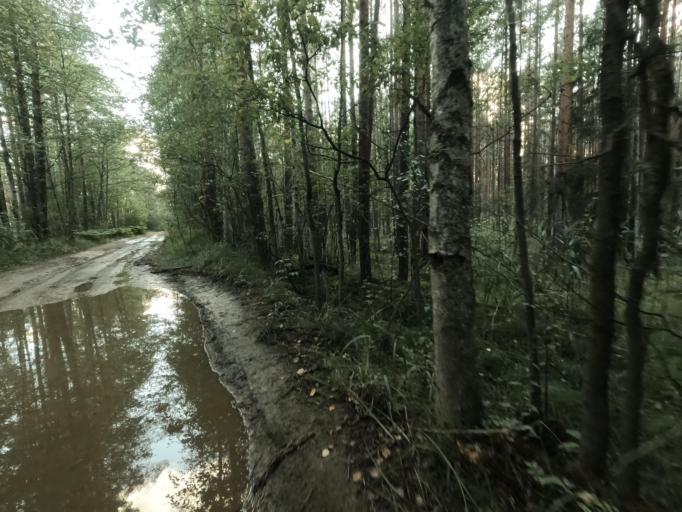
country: RU
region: Leningrad
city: Otradnoye
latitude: 59.8470
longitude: 30.7930
